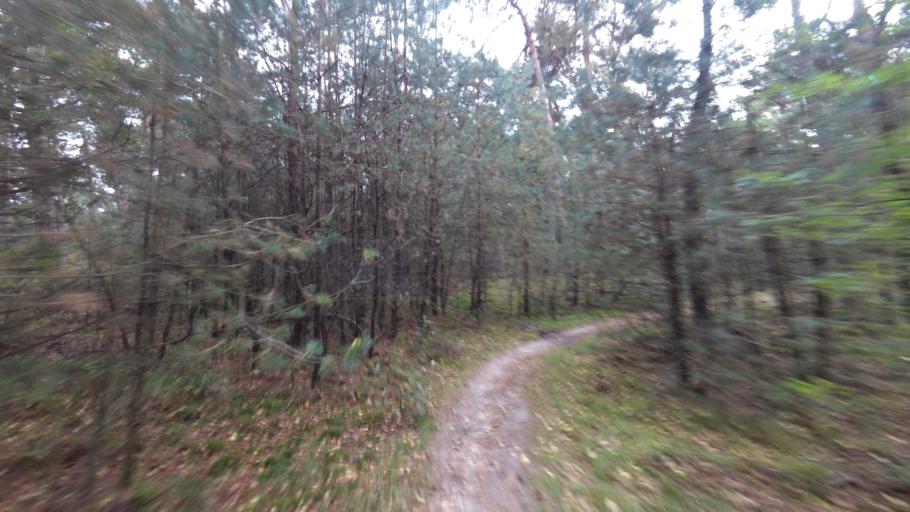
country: NL
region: Gelderland
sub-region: Gemeente Barneveld
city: Stroe
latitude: 52.1723
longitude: 5.7228
